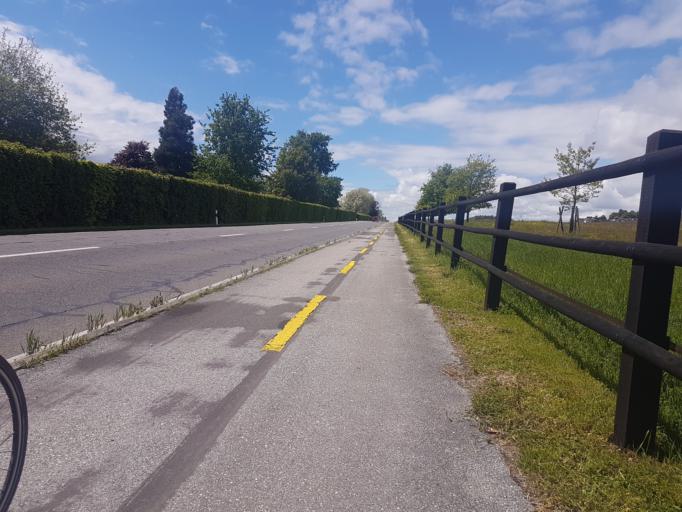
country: CH
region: Vaud
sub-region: Nyon District
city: Rolle
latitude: 46.4409
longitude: 6.3151
